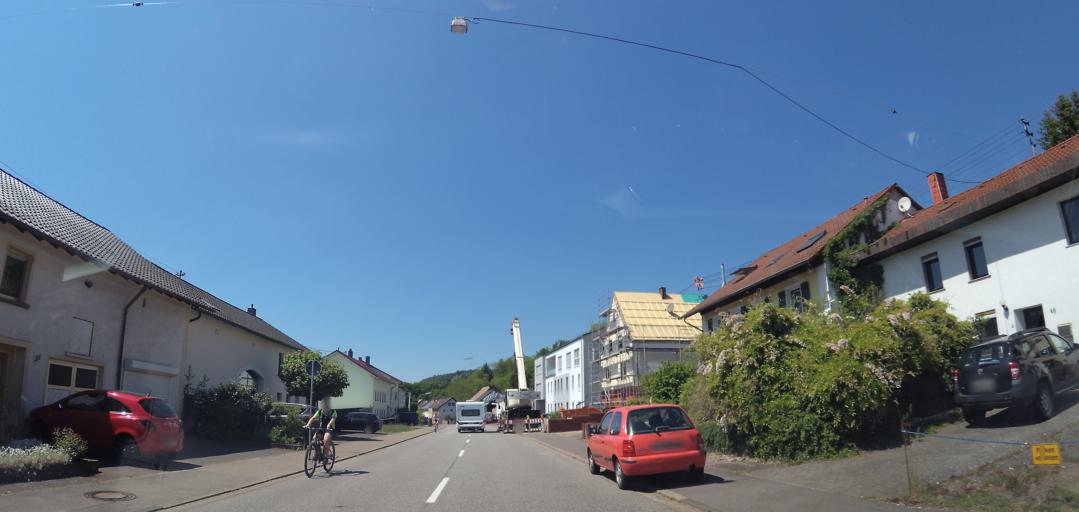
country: DE
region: Saarland
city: Losheim
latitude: 49.4548
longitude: 6.7828
